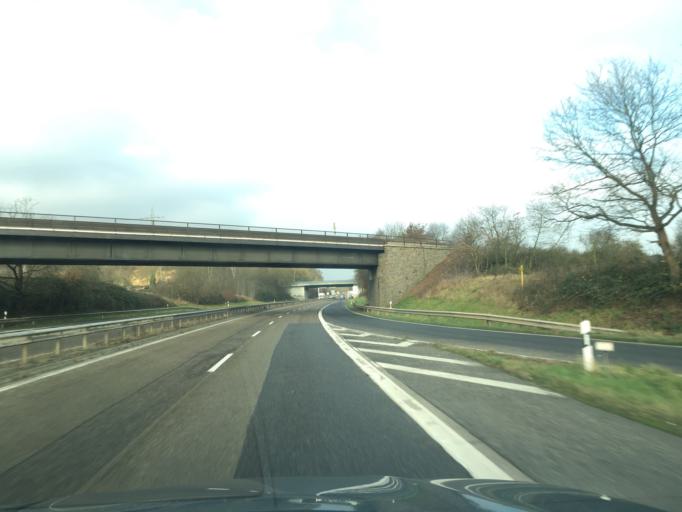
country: DE
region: Rheinland-Pfalz
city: Sinzig
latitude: 50.5585
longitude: 7.2469
